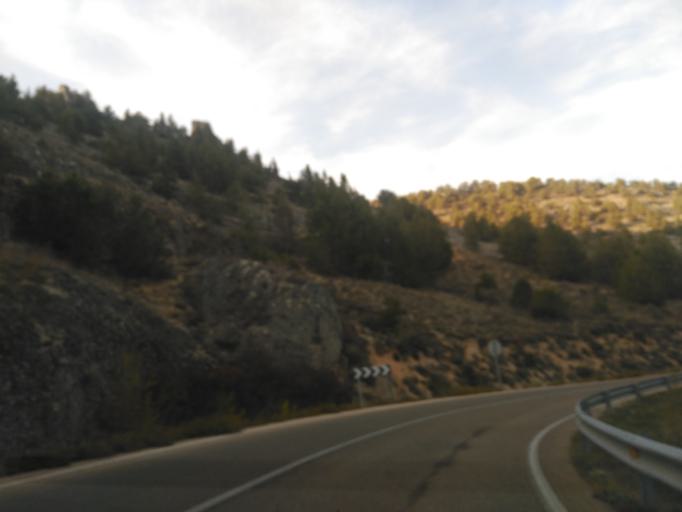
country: ES
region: Castille and Leon
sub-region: Provincia de Soria
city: Ucero
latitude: 41.7212
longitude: -3.0506
